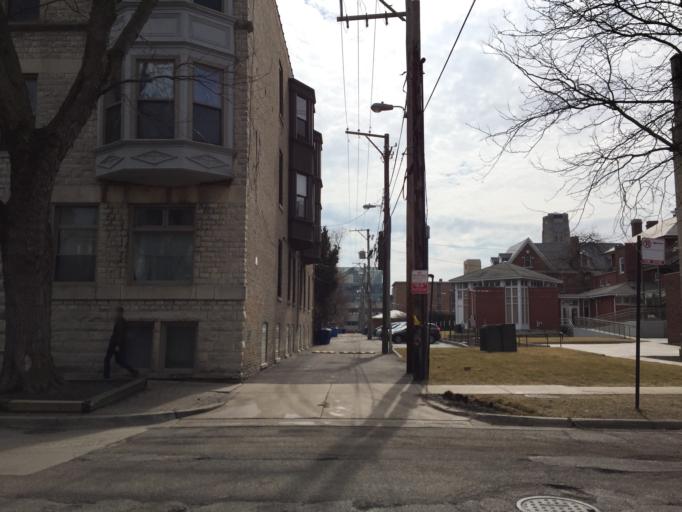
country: US
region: Illinois
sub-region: Cook County
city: Chicago
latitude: 41.7915
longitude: -87.5957
